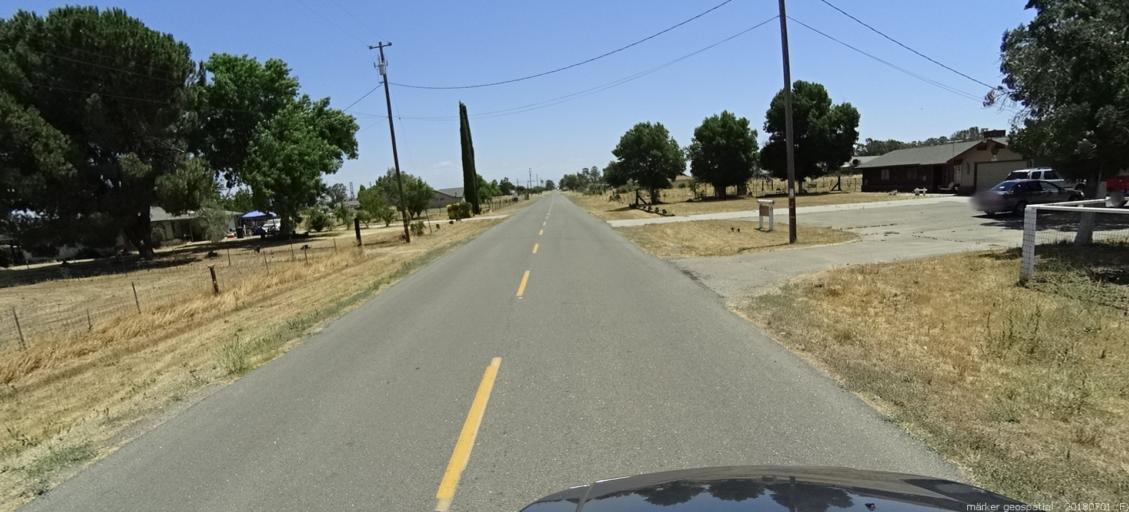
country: US
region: California
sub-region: Madera County
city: Madera Acres
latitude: 37.0468
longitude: -119.9922
